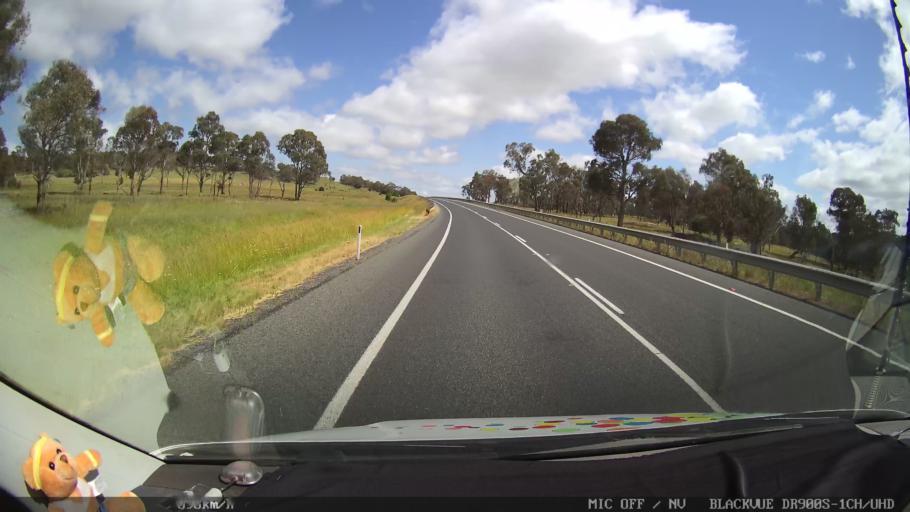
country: AU
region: New South Wales
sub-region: Glen Innes Severn
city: Glen Innes
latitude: -29.8940
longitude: 151.7339
